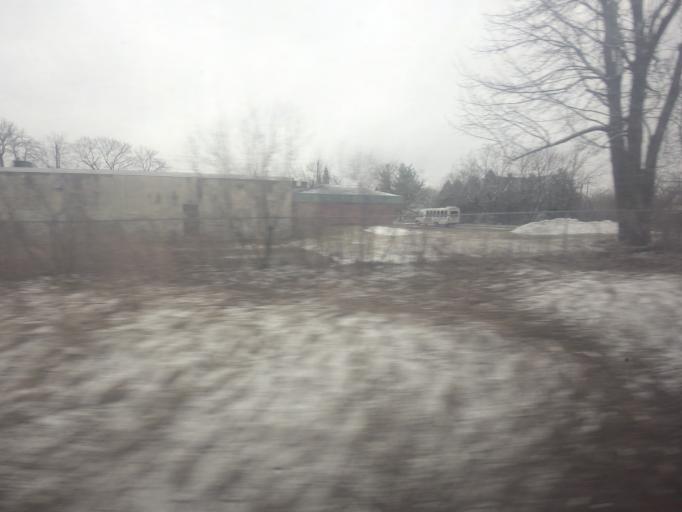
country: CA
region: Ontario
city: Brockville
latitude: 44.6023
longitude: -75.6917
